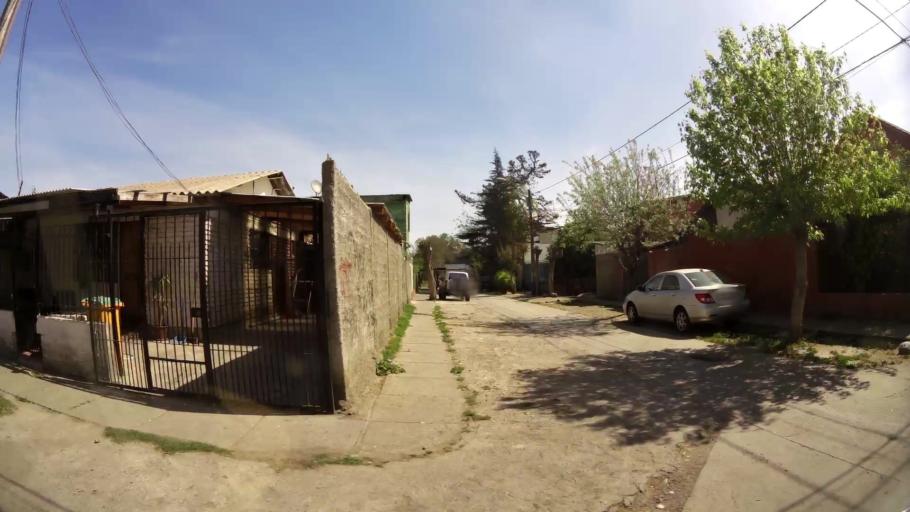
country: CL
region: Santiago Metropolitan
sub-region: Provincia de Maipo
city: San Bernardo
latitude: -33.5240
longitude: -70.7011
